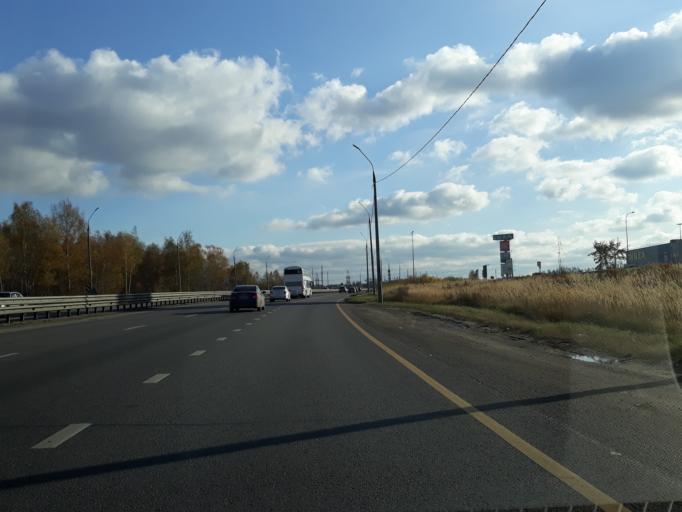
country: RU
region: Nizjnij Novgorod
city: Afonino
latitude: 56.2282
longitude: 44.0739
